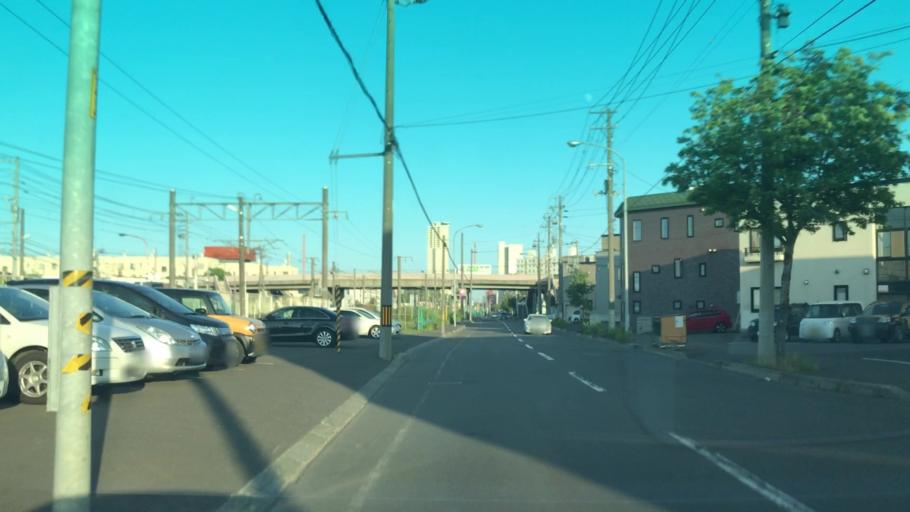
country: JP
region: Hokkaido
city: Sapporo
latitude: 43.0890
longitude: 141.2947
